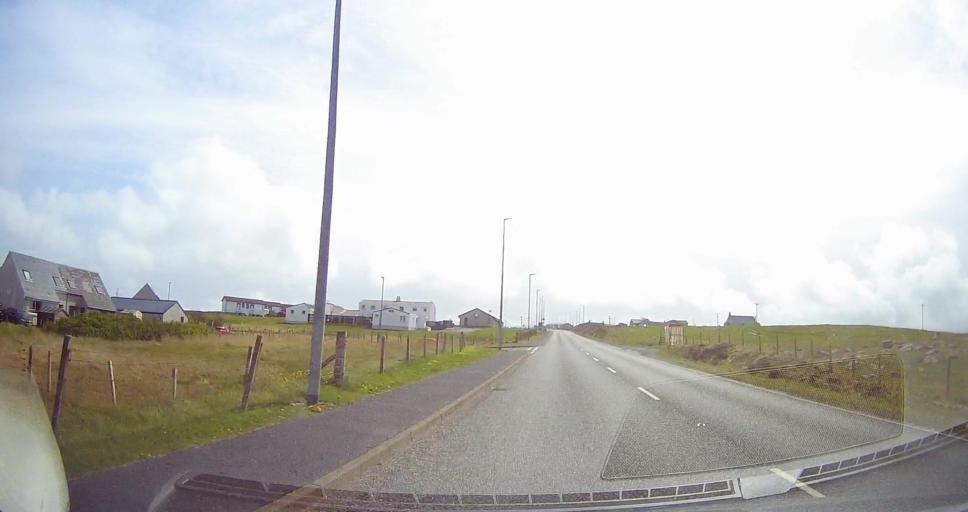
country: GB
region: Scotland
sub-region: Shetland Islands
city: Sandwick
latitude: 59.9237
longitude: -1.2977
